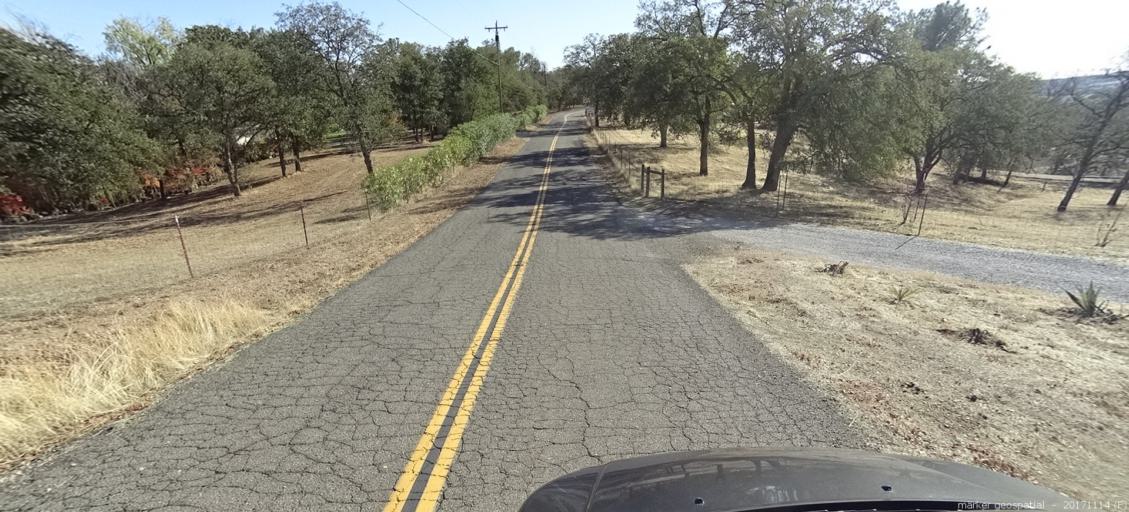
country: US
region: California
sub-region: Shasta County
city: Anderson
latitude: 40.4049
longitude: -122.4099
